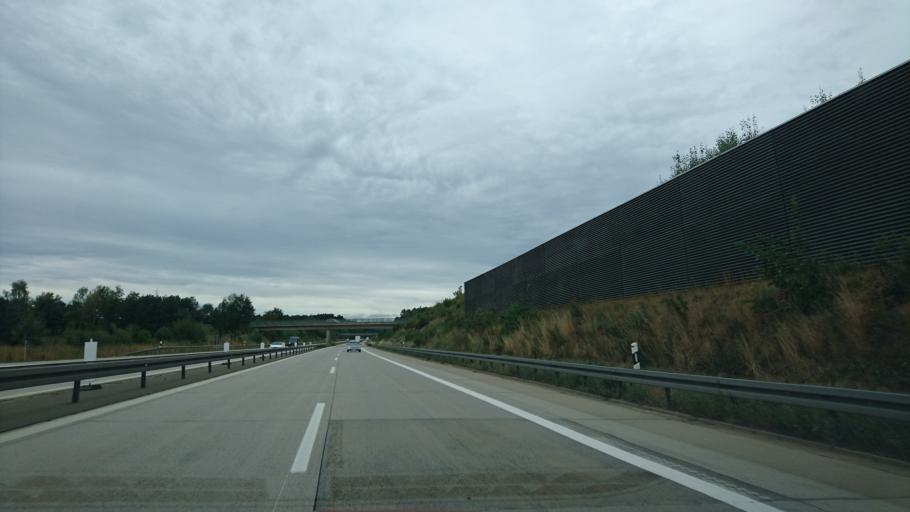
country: DE
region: Bavaria
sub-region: Upper Palatinate
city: Wernberg-Koblitz
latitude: 49.5378
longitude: 12.1349
